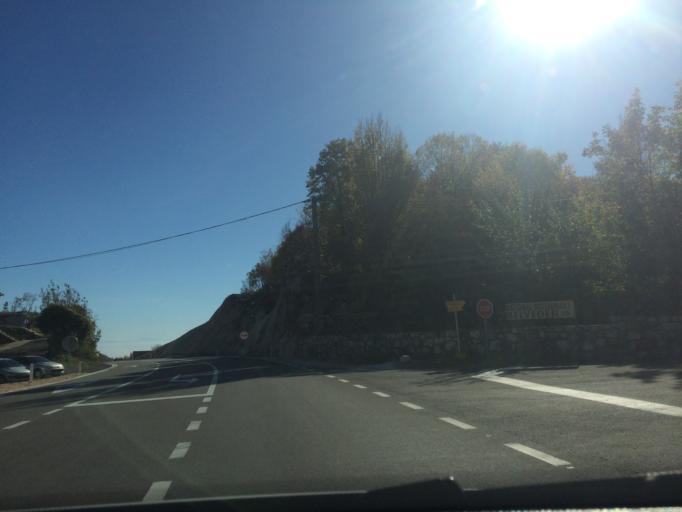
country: ME
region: Cetinje
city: Cetinje
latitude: 42.3865
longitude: 18.9398
